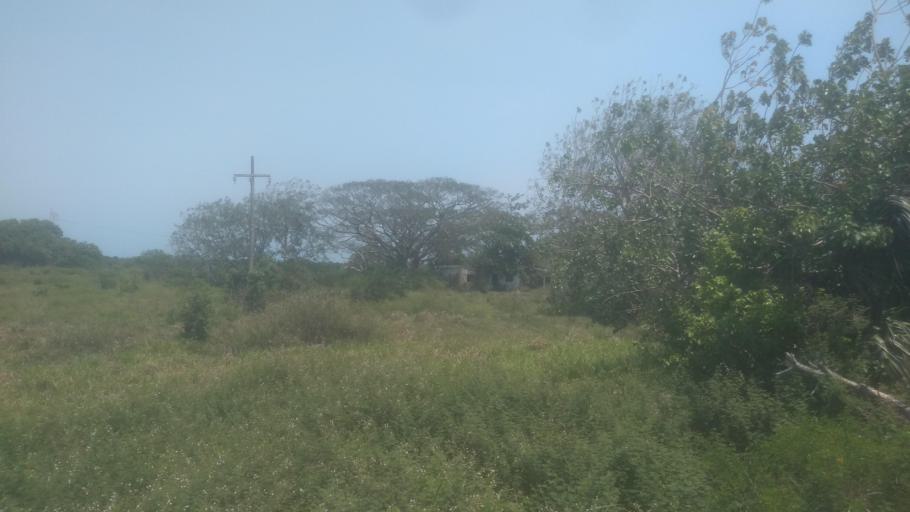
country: MX
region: Veracruz
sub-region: Medellin
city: Fraccionamiento Arboledas San Ramon
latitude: 19.1026
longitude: -96.1493
